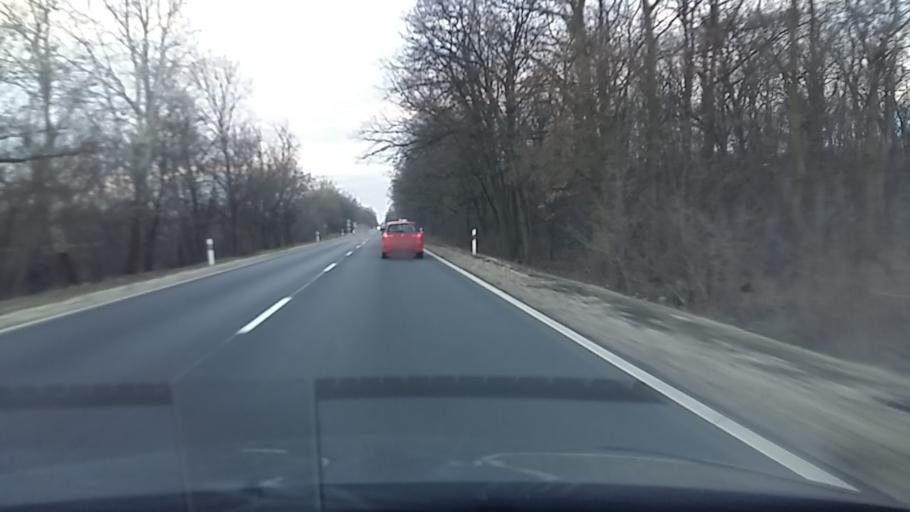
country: HU
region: Hajdu-Bihar
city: Debrecen
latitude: 47.5700
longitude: 21.6528
